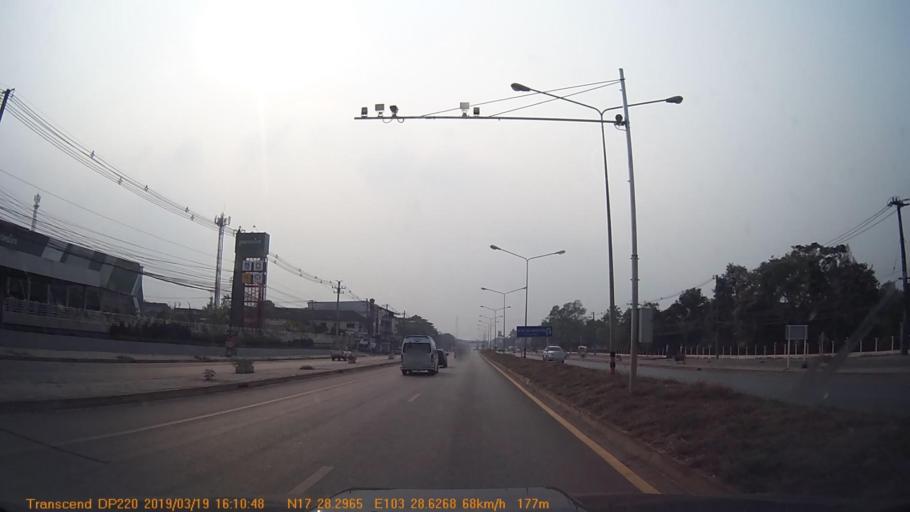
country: TH
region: Sakon Nakhon
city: Sawang Daen Din
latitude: 17.4717
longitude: 103.4766
